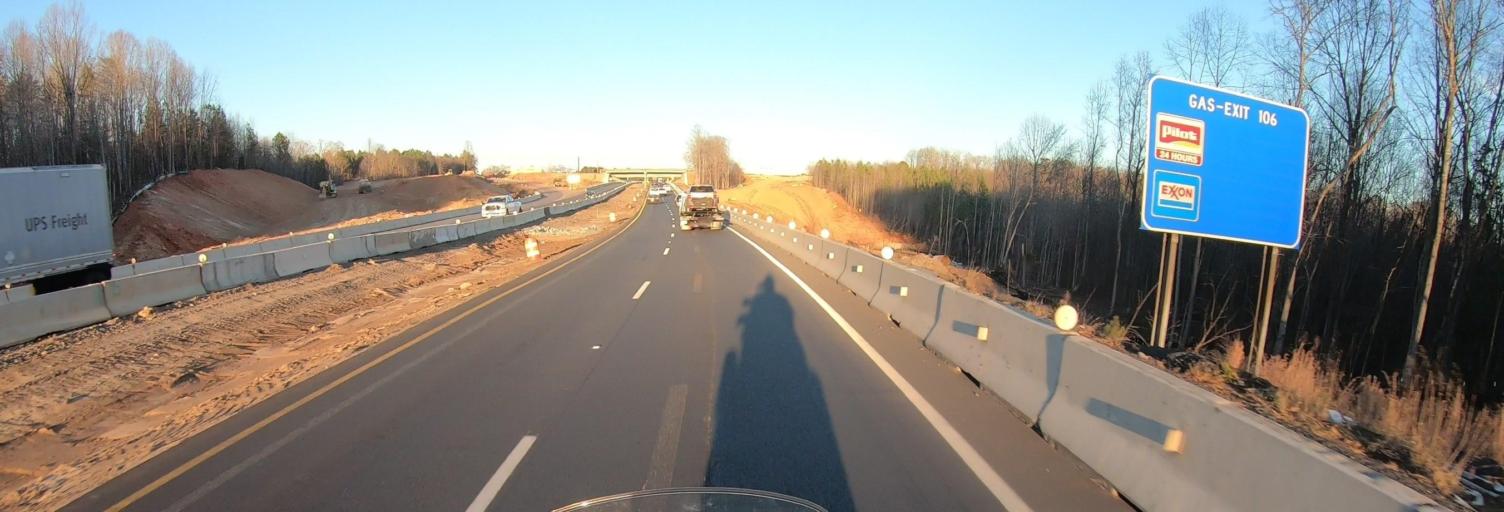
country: US
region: South Carolina
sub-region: Cherokee County
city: Blacksburg
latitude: 35.1601
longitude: -81.4579
